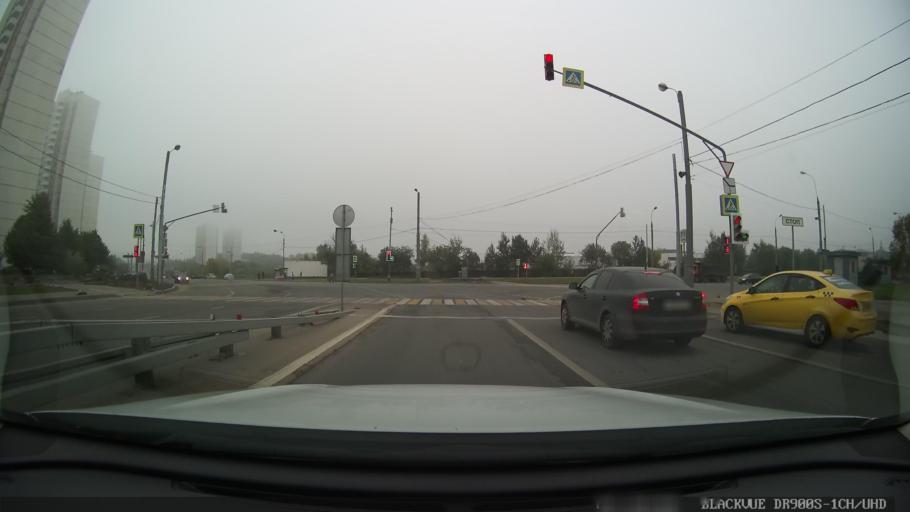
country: RU
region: Moscow
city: Solntsevo
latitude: 55.6400
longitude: 37.3675
